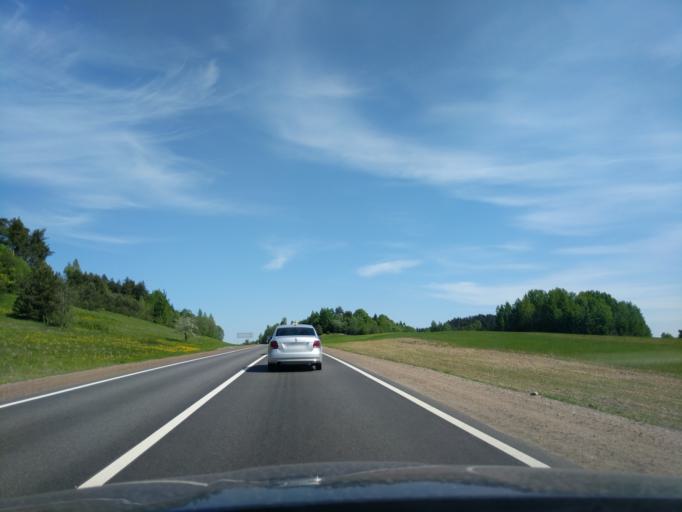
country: BY
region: Minsk
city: Bal'shavik
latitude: 54.0926
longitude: 27.5353
